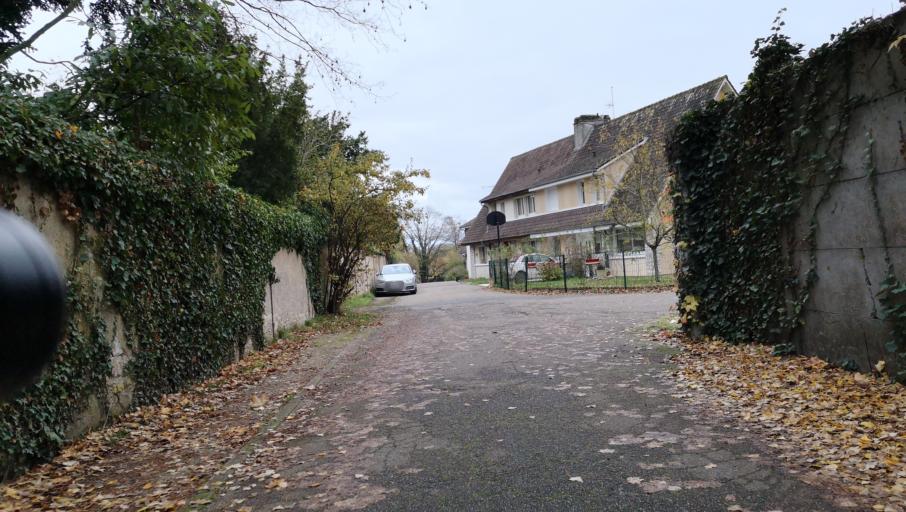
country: FR
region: Centre
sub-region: Departement du Loiret
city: Semoy
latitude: 47.9052
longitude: 1.9493
